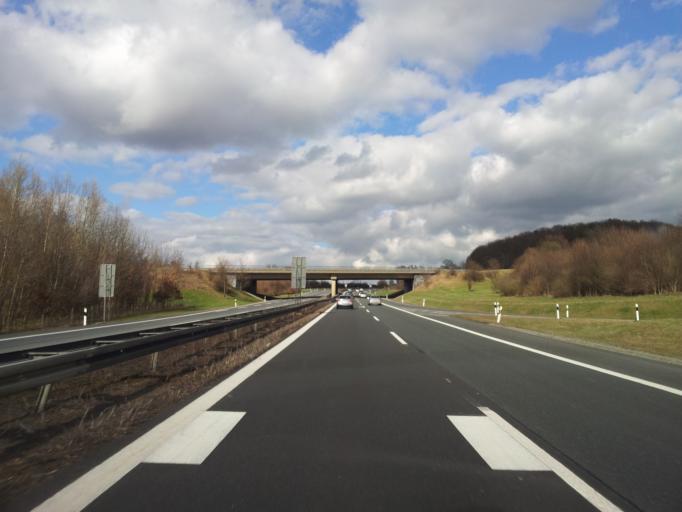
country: DE
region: Saxony
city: Neuensalz
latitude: 50.5003
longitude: 12.2015
